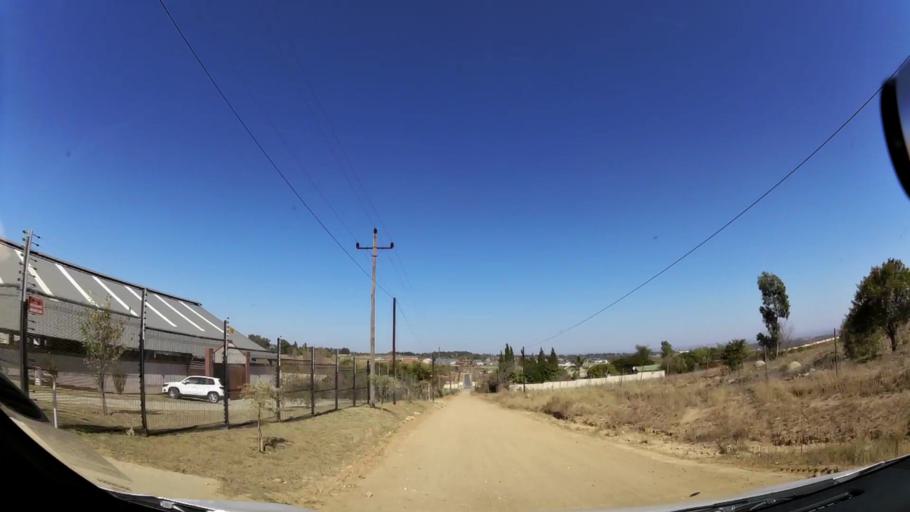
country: ZA
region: Gauteng
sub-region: City of Johannesburg Metropolitan Municipality
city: Midrand
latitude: -25.9456
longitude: 28.0842
